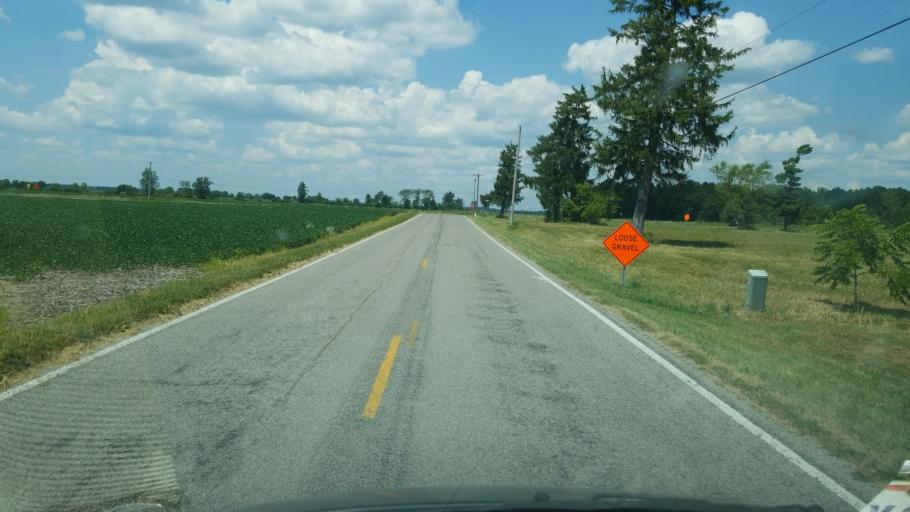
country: US
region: Ohio
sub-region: Champaign County
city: Mechanicsburg
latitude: 40.1166
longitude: -83.4697
